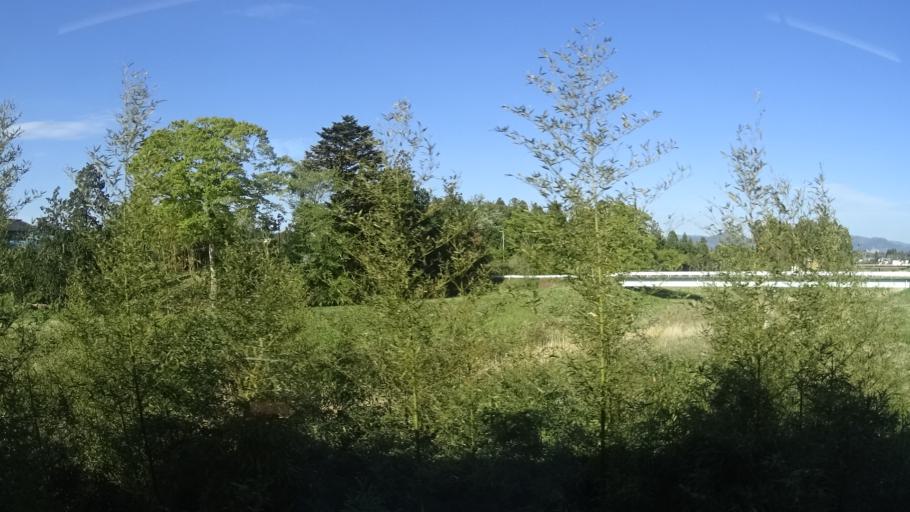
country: JP
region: Fukushima
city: Namie
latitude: 37.6014
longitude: 140.9950
